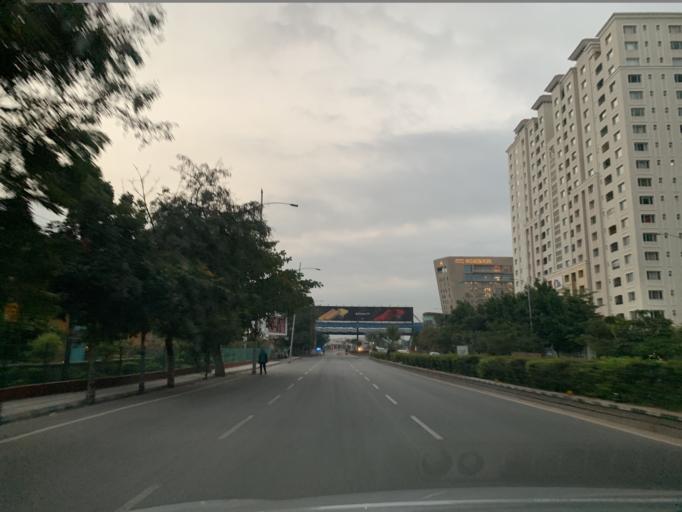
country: IN
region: Telangana
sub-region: Rangareddi
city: Kukatpalli
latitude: 17.4348
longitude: 78.3835
